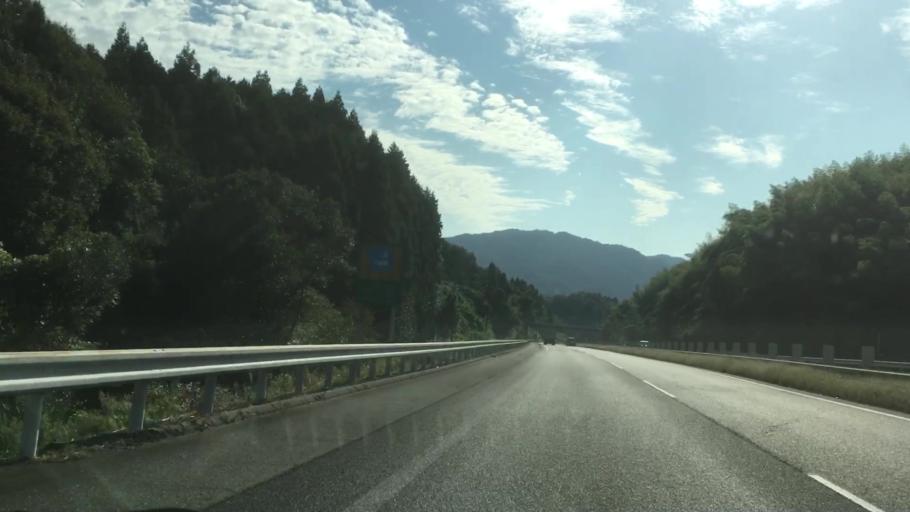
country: JP
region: Yamaguchi
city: Hikari
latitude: 34.0325
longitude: 131.9675
